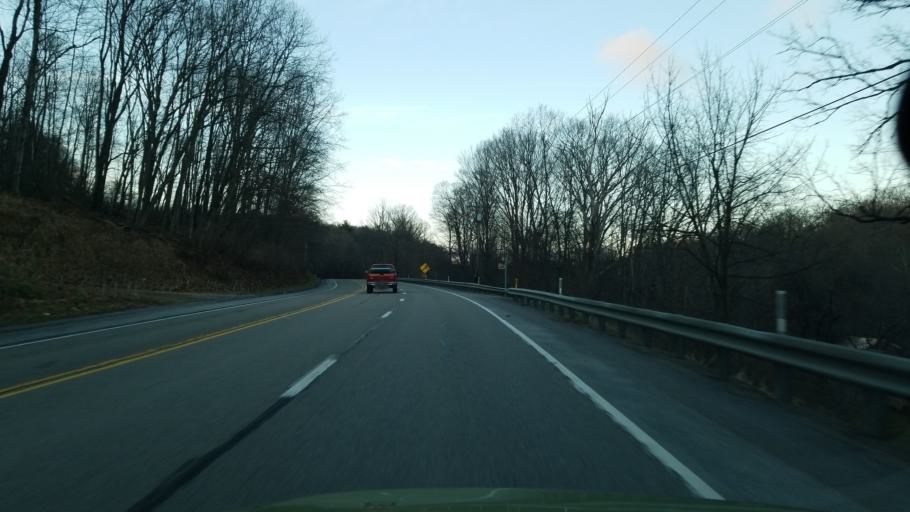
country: US
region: Pennsylvania
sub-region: Jefferson County
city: Punxsutawney
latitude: 40.8291
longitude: -79.0387
